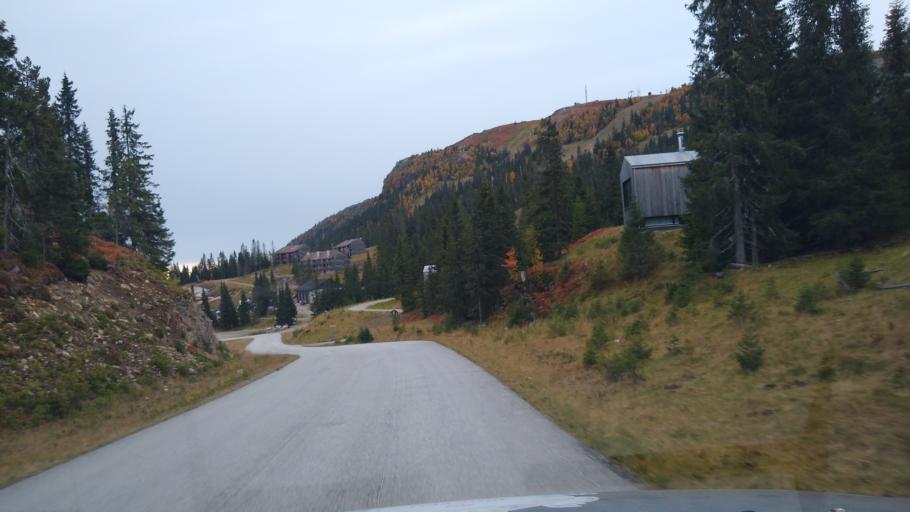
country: NO
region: Oppland
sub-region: Ringebu
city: Ringebu
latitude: 61.4756
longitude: 10.1284
